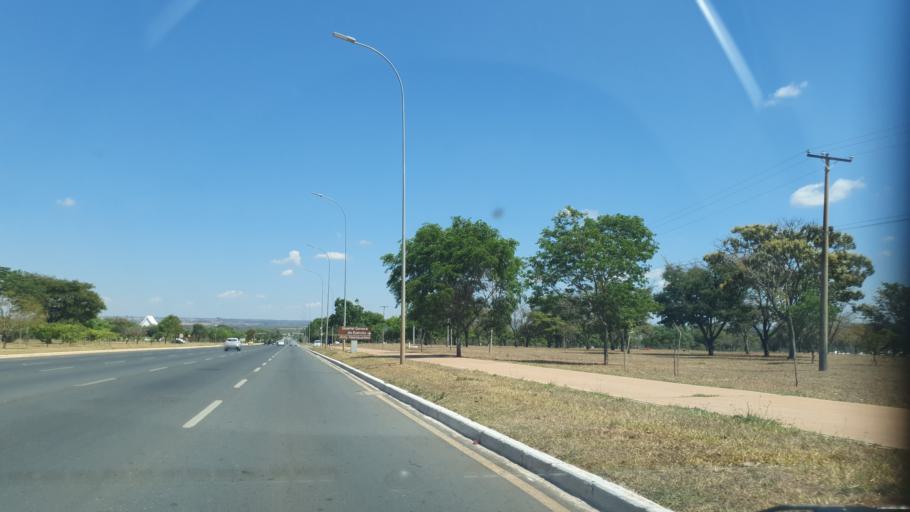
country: BR
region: Federal District
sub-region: Brasilia
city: Brasilia
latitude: -15.7814
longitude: -47.9188
